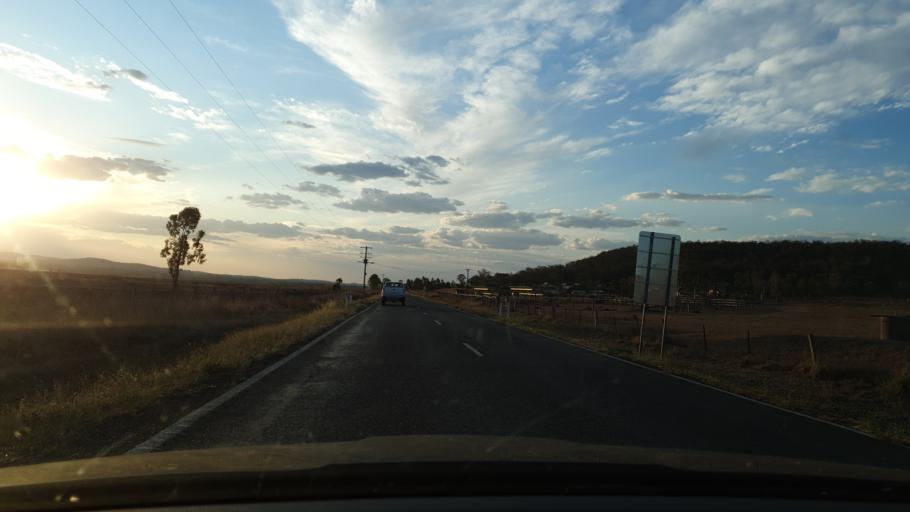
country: AU
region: Queensland
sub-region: Southern Downs
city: Warwick
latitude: -28.1855
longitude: 152.0043
